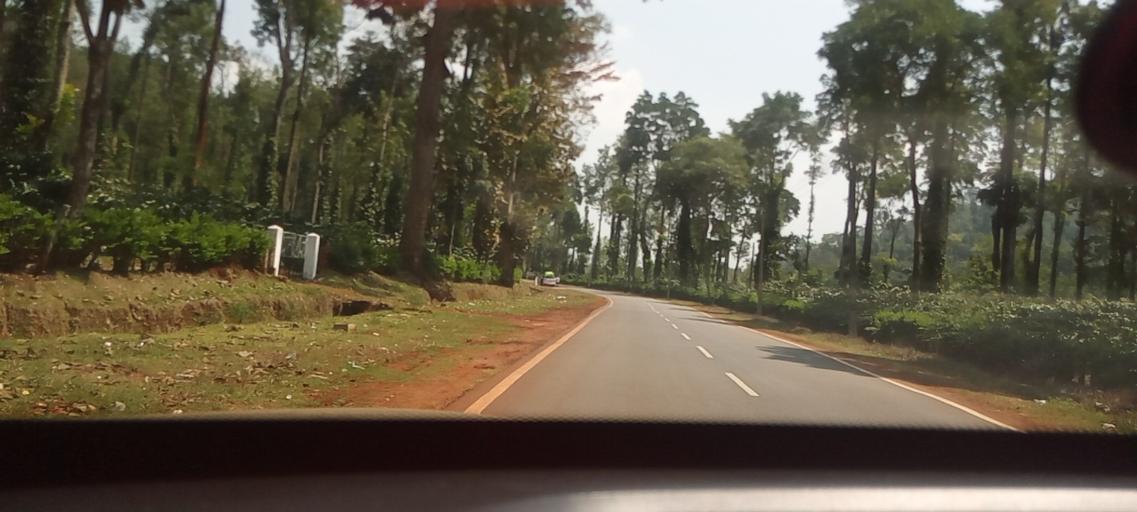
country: IN
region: Karnataka
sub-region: Chikmagalur
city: Koppa
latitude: 13.3502
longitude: 75.4763
